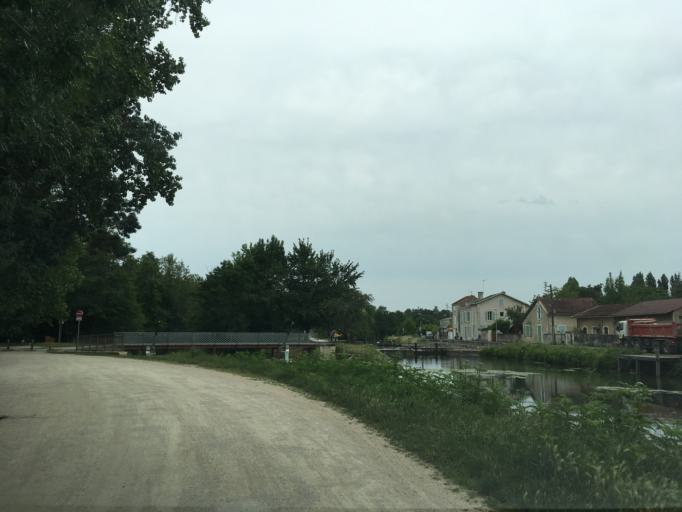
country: FR
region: Poitou-Charentes
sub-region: Departement des Deux-Sevres
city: Niort
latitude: 46.3288
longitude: -0.4772
